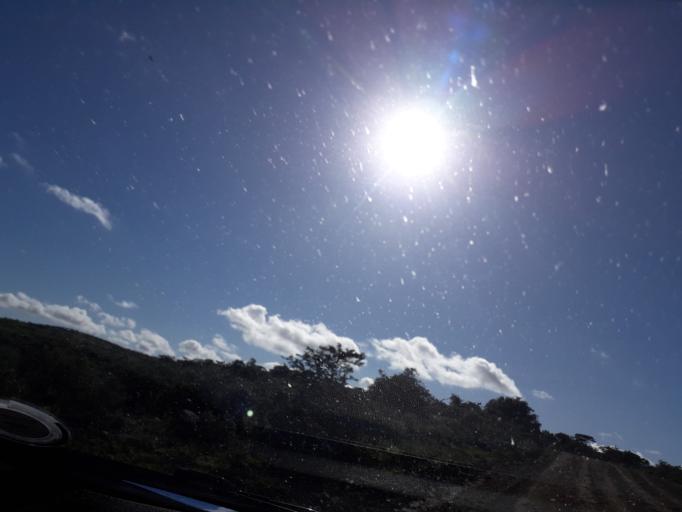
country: ZA
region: Eastern Cape
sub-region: Buffalo City Metropolitan Municipality
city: Bhisho
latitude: -33.1239
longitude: 27.4503
